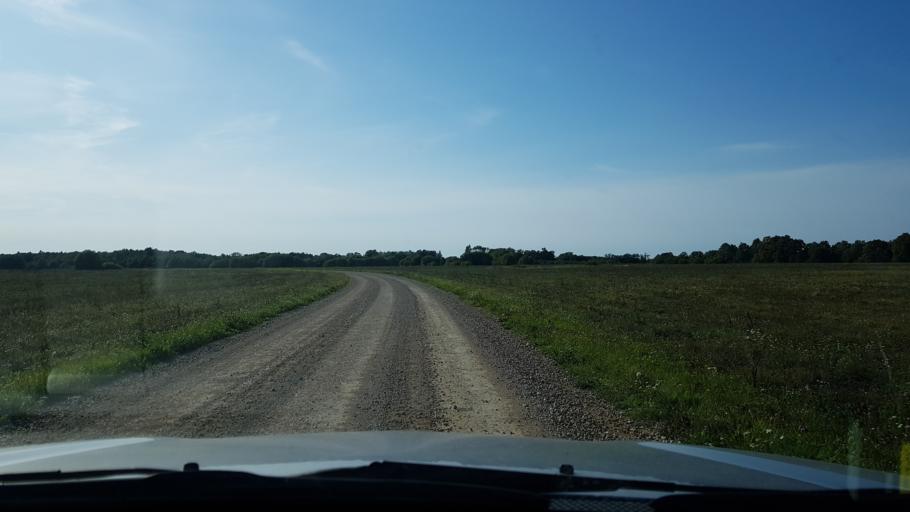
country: EE
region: Ida-Virumaa
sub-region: Narva-Joesuu linn
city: Narva-Joesuu
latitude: 59.4078
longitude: 28.0028
